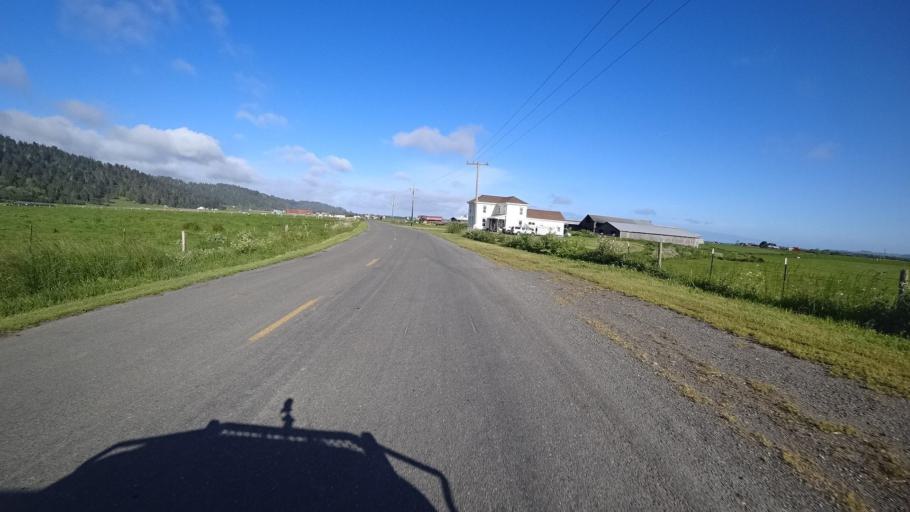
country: US
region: California
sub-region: Humboldt County
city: Ferndale
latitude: 40.5707
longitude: -124.2230
